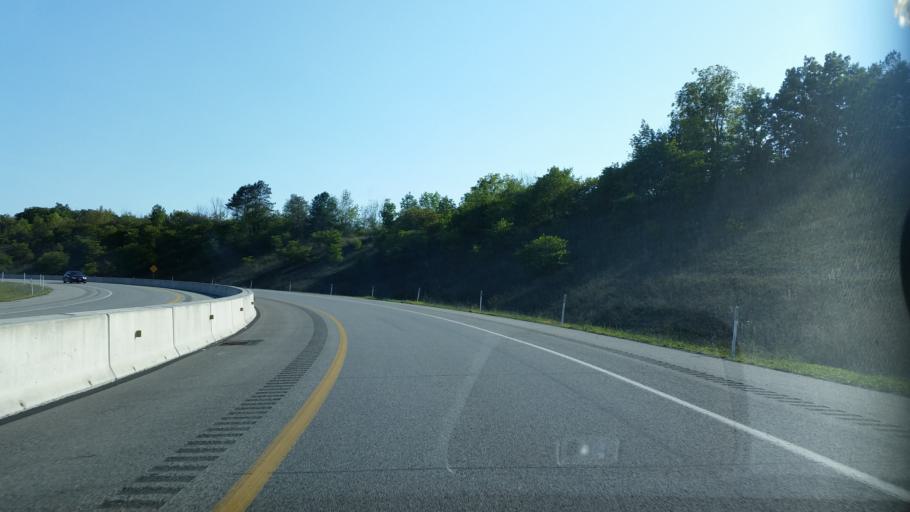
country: US
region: Pennsylvania
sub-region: Bedford County
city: Bedford
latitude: 40.0577
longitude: -78.5202
